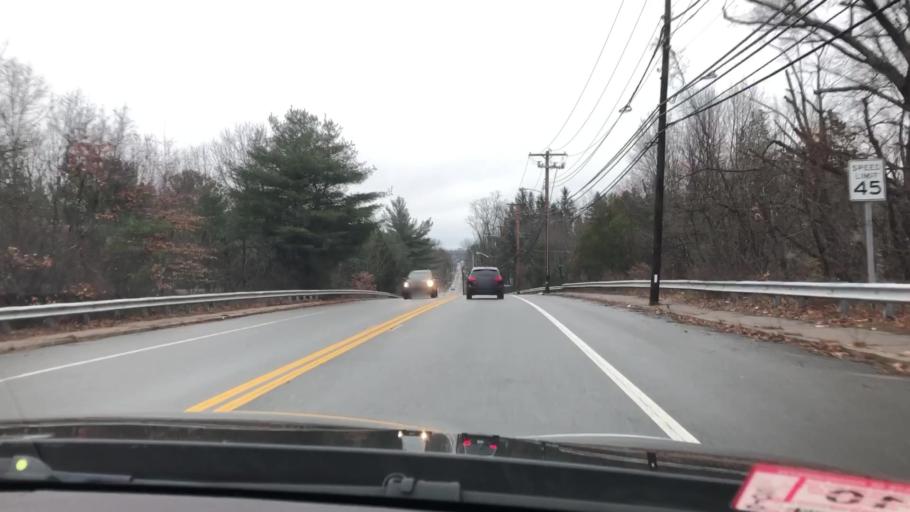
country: US
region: Massachusetts
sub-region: Norfolk County
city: Walpole
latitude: 42.1372
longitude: -71.2591
